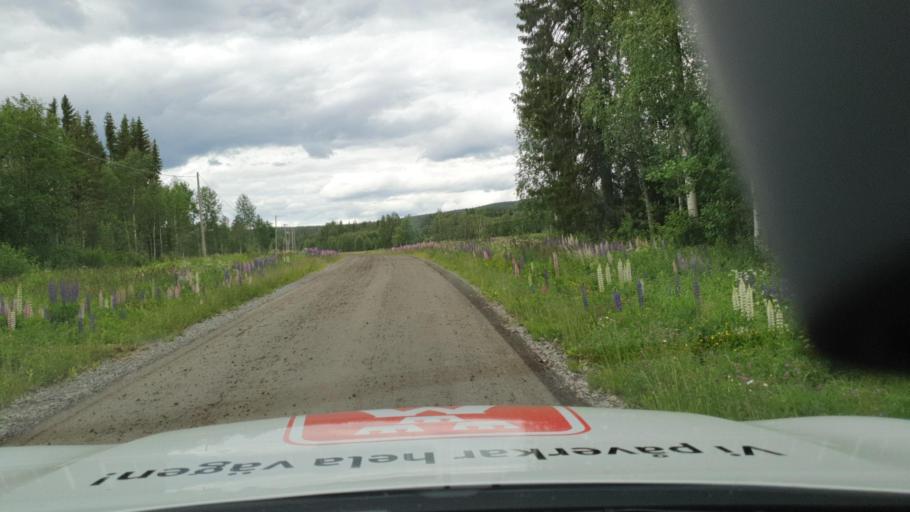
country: SE
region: Vaesterbotten
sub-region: Bjurholms Kommun
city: Bjurholm
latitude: 63.7979
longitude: 19.0864
